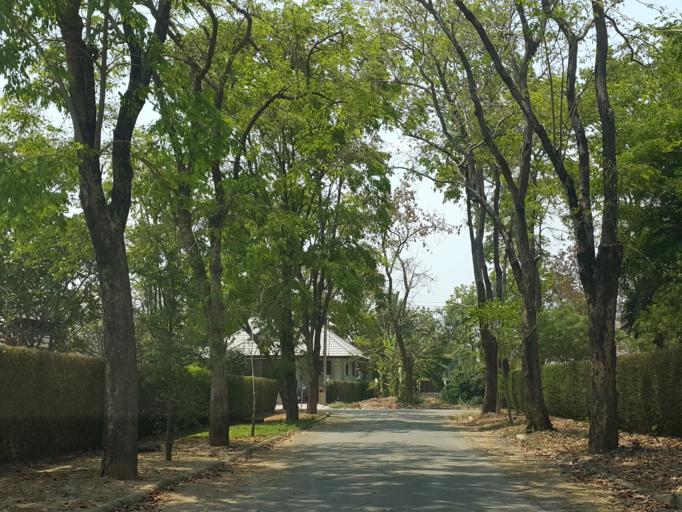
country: TH
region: Chiang Mai
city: Saraphi
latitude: 18.7273
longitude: 98.9759
